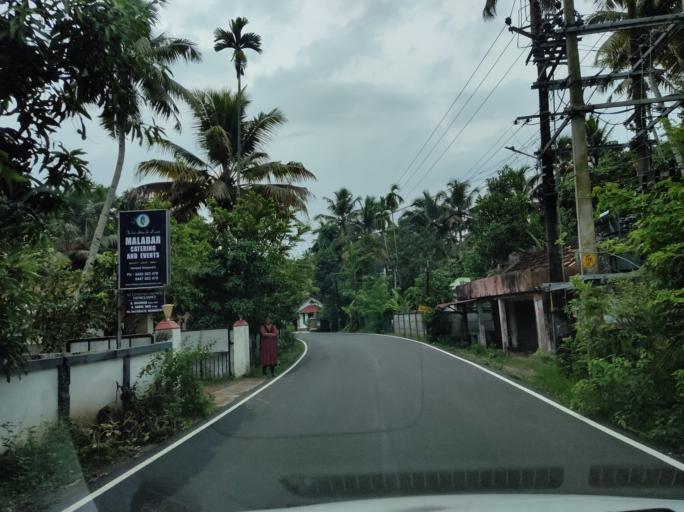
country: IN
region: Kerala
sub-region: Alappuzha
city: Kayankulam
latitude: 9.2688
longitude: 76.4034
